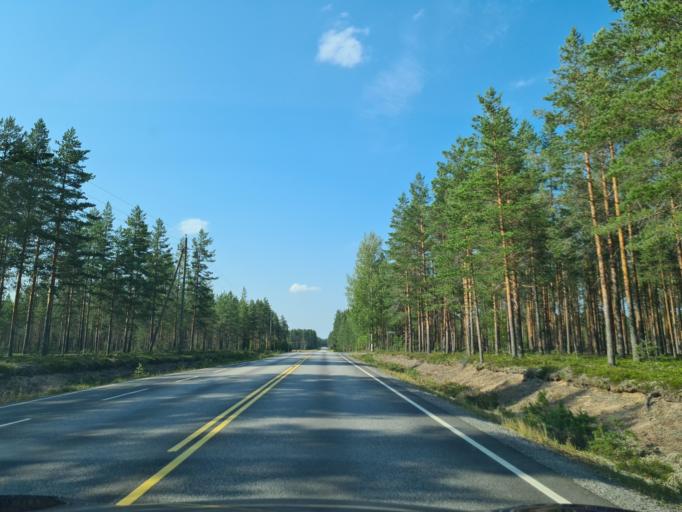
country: FI
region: Satakunta
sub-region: Pohjois-Satakunta
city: Karvia
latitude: 62.0639
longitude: 22.5109
